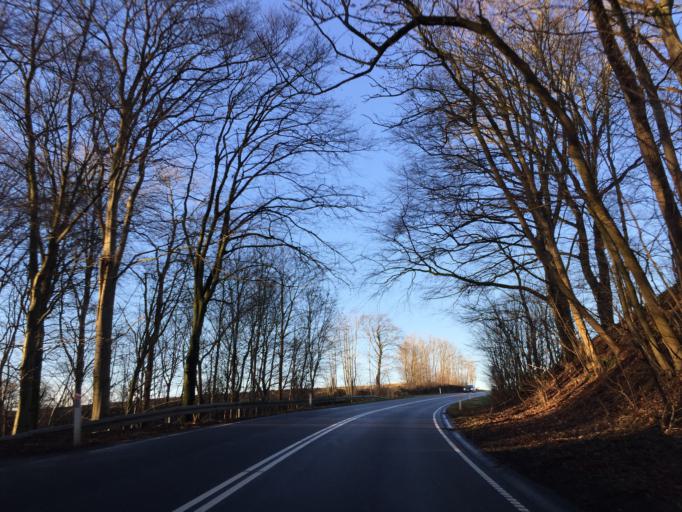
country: DK
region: Central Jutland
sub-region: Skanderborg Kommune
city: Skanderborg
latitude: 56.0606
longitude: 9.9034
